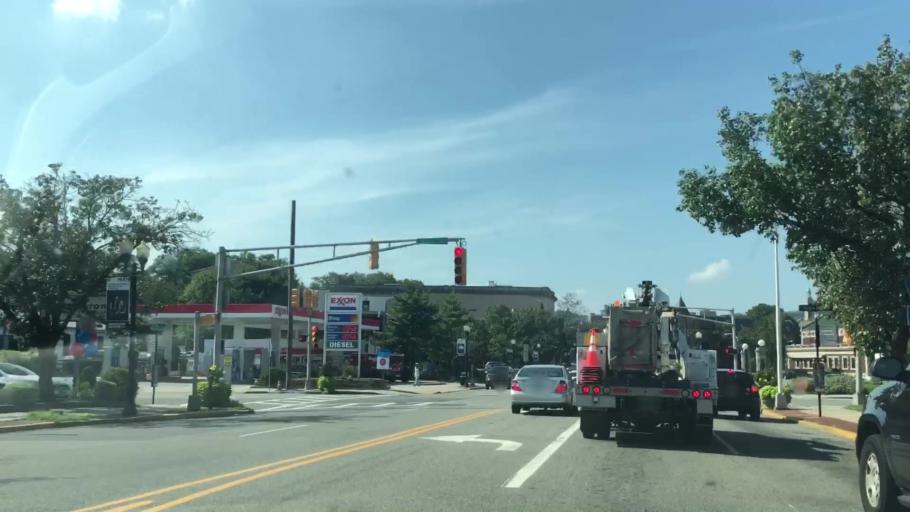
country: US
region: New Jersey
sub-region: Essex County
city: Glen Ridge
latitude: 40.8098
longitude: -74.2127
